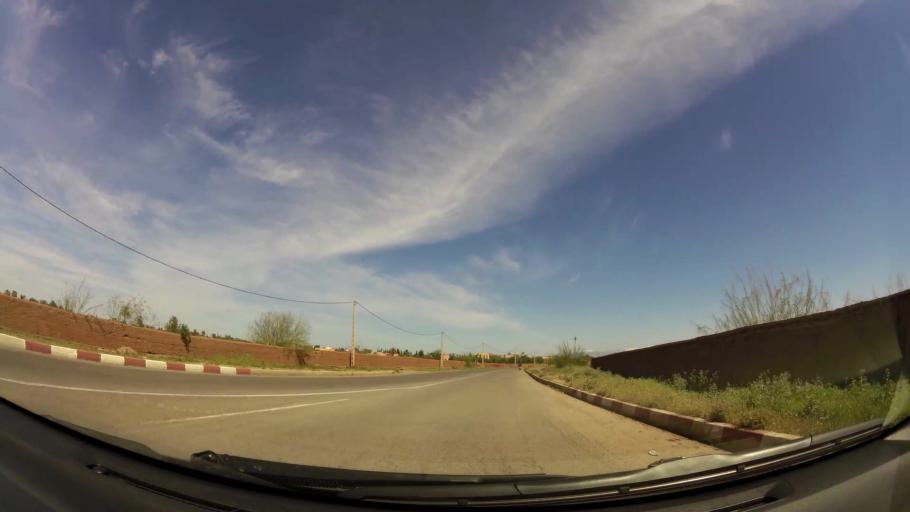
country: MA
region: Marrakech-Tensift-Al Haouz
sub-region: Marrakech
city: Marrakesh
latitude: 31.6125
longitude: -7.9454
